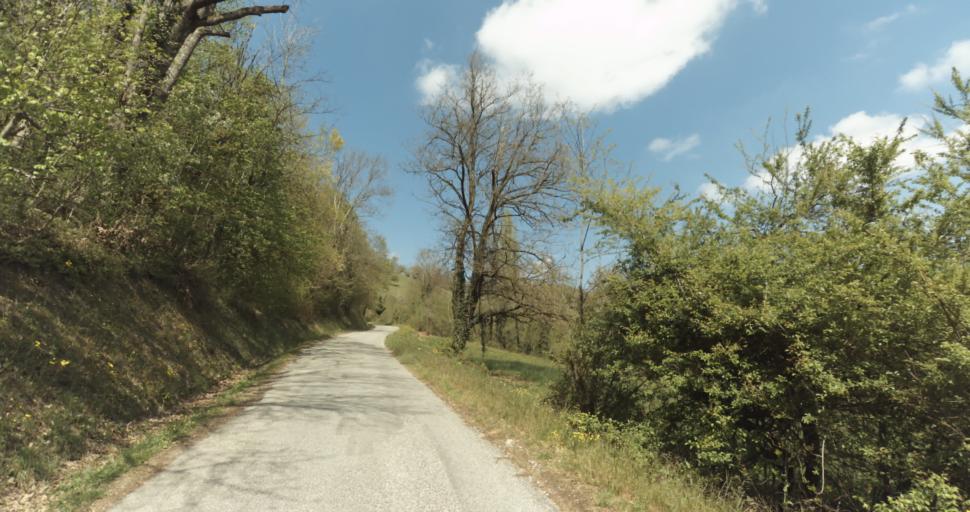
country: FR
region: Rhone-Alpes
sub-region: Departement de l'Isere
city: Saint-Marcellin
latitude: 45.1558
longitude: 5.3093
